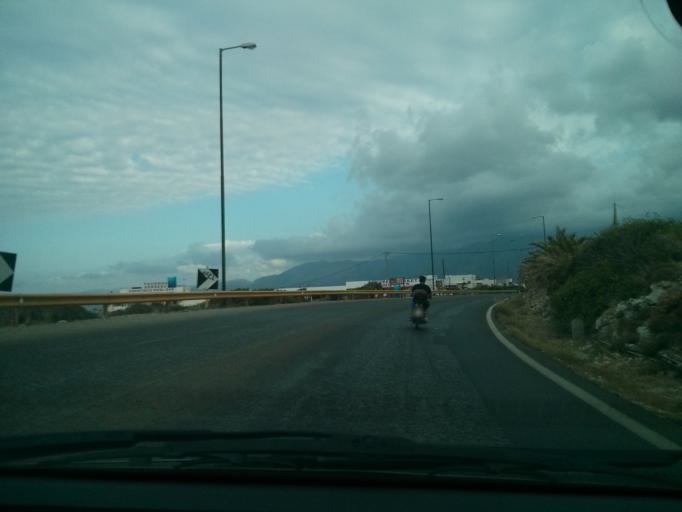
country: GR
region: Crete
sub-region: Nomos Irakleiou
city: Stalis
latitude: 35.3042
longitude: 25.4171
